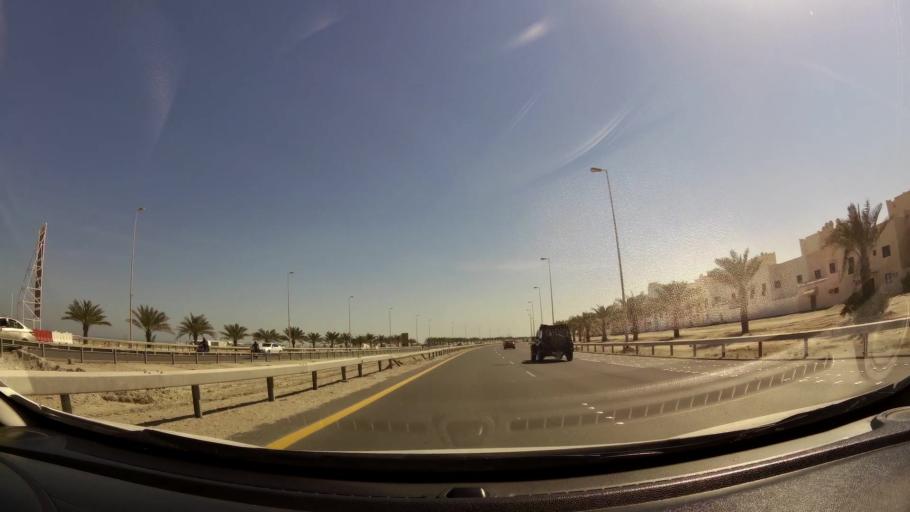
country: BH
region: Muharraq
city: Al Hadd
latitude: 26.2702
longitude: 50.6616
